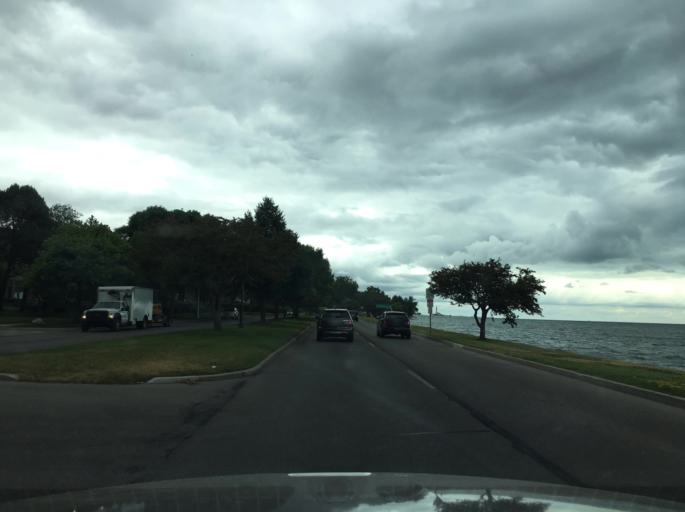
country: US
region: Michigan
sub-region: Wayne County
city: Grosse Pointe Farms
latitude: 42.4122
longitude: -82.8848
